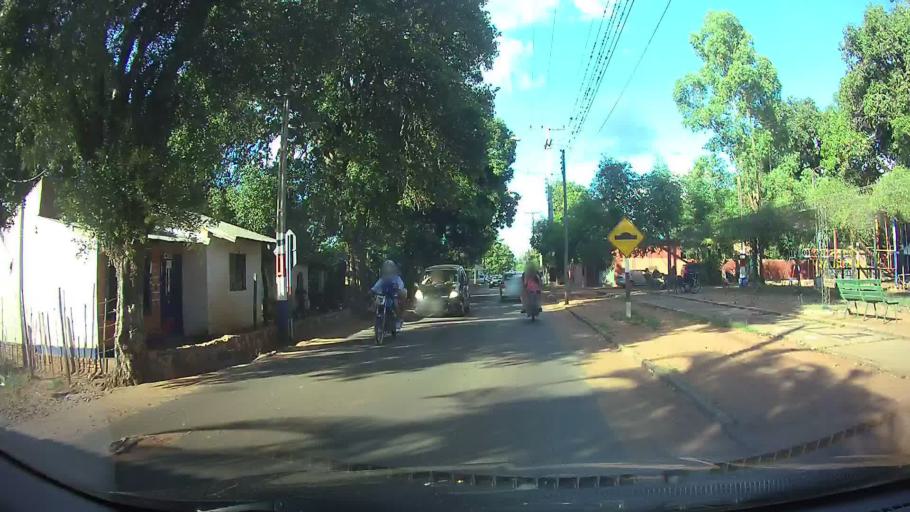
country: PY
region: Central
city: Aregua
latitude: -25.2893
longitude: -57.4401
